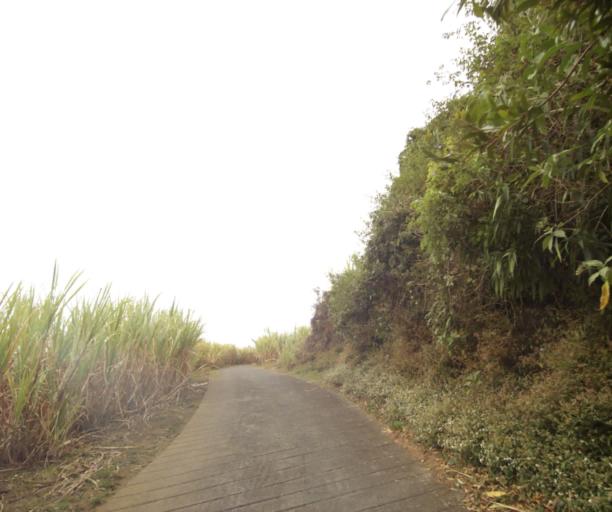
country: RE
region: Reunion
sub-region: Reunion
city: Saint-Paul
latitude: -21.0257
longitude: 55.3225
